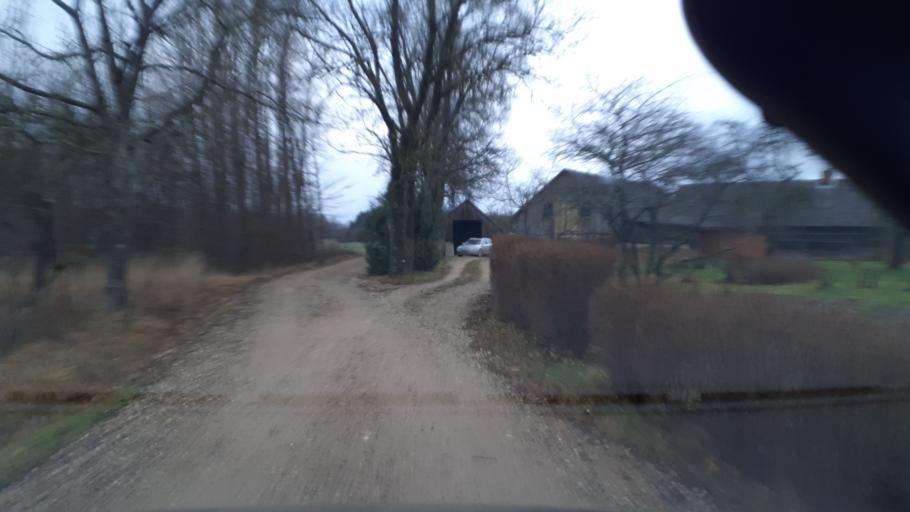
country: LV
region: Alsunga
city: Alsunga
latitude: 56.8786
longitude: 21.6859
